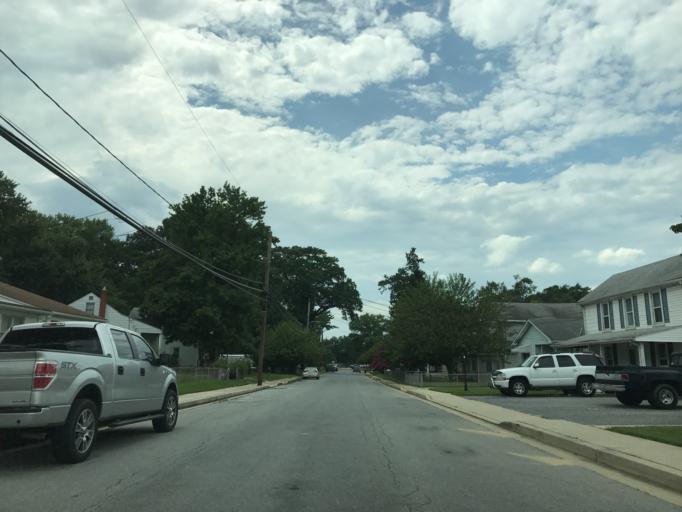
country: US
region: Maryland
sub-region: Baltimore County
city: Essex
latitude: 39.3112
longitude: -76.4828
